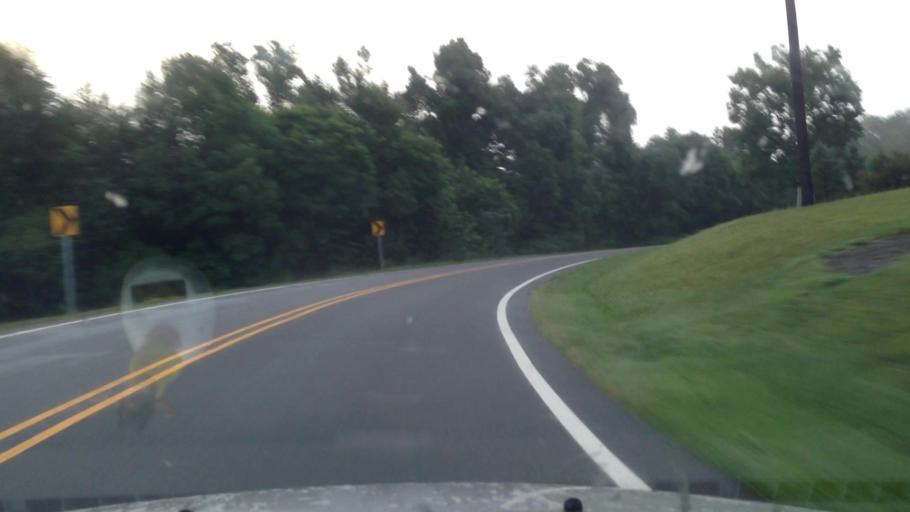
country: US
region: North Carolina
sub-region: Forsyth County
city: Kernersville
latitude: 36.1548
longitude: -80.0960
